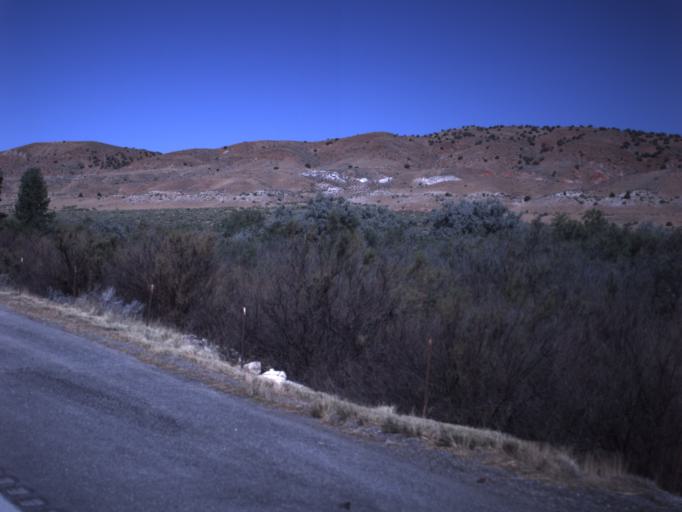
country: US
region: Utah
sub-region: Sanpete County
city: Gunnison
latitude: 39.1668
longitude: -111.7277
